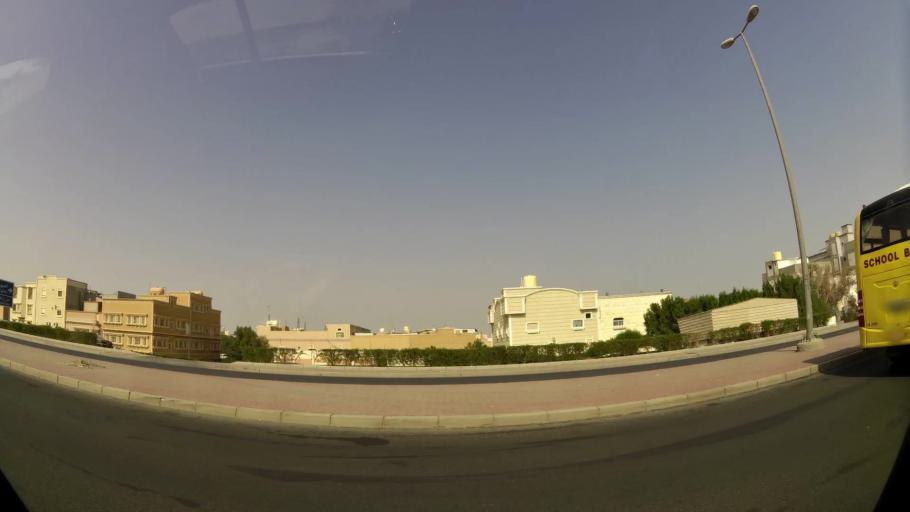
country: KW
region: Muhafazat al Jahra'
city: Al Jahra'
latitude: 29.3206
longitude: 47.6551
